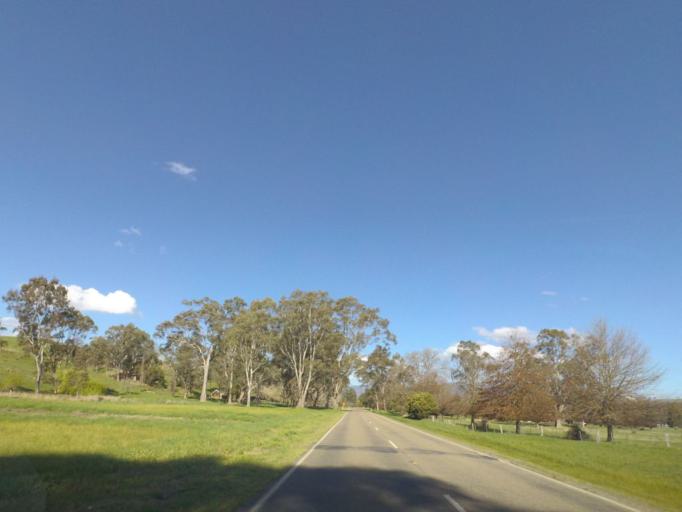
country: AU
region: Victoria
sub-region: Murrindindi
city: Alexandra
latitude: -37.2317
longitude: 145.7665
